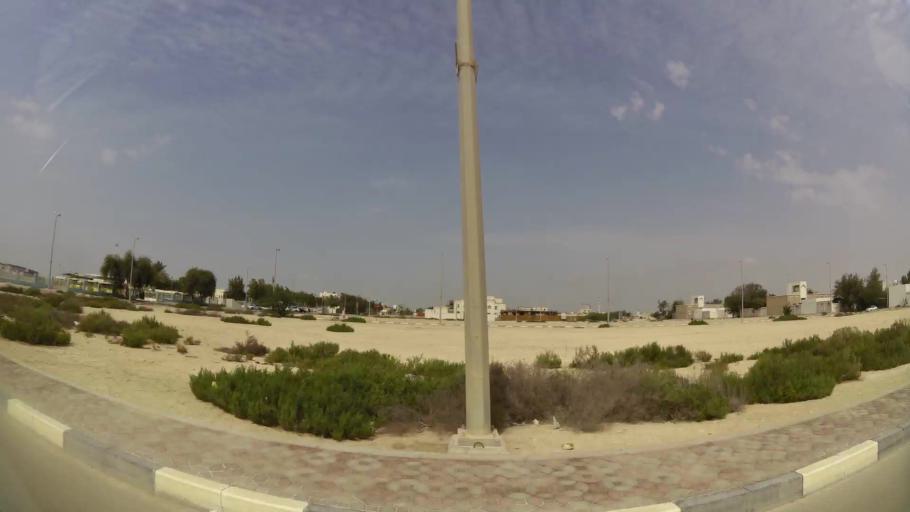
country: AE
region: Abu Dhabi
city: Abu Dhabi
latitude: 24.5238
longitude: 54.6863
